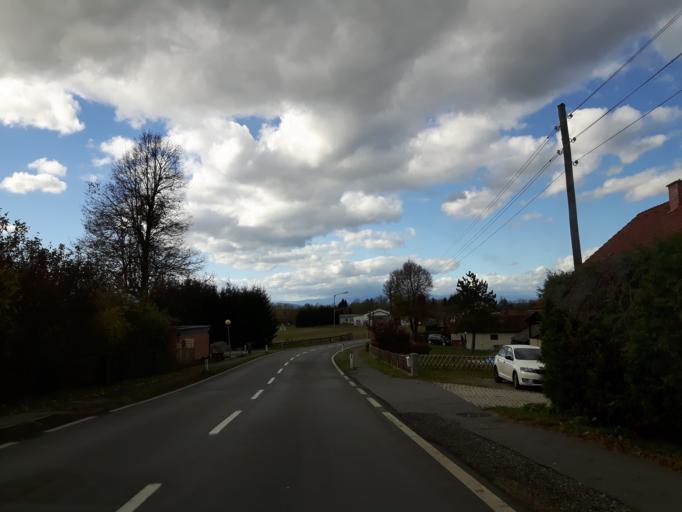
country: AT
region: Styria
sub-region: Politischer Bezirk Leibnitz
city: Ragnitz
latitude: 46.8353
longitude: 15.5986
